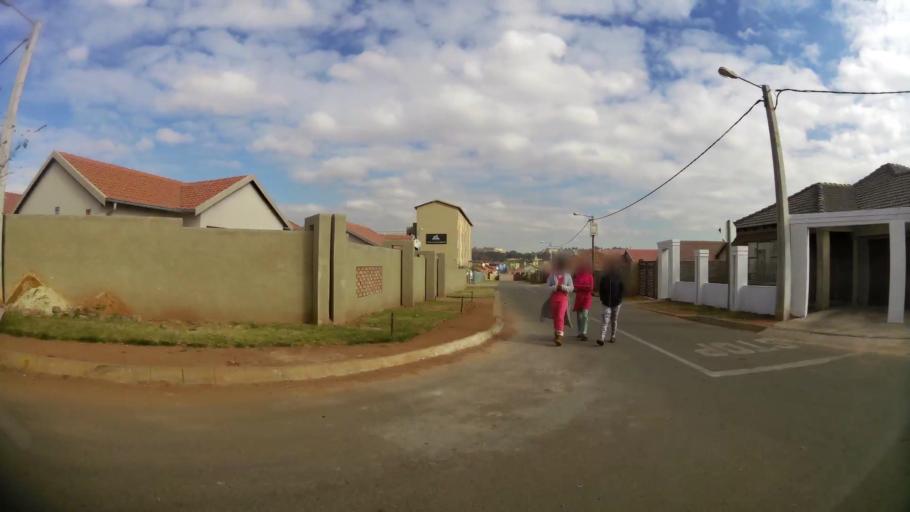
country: ZA
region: Gauteng
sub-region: City of Johannesburg Metropolitan Municipality
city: Roodepoort
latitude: -26.2036
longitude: 27.9139
